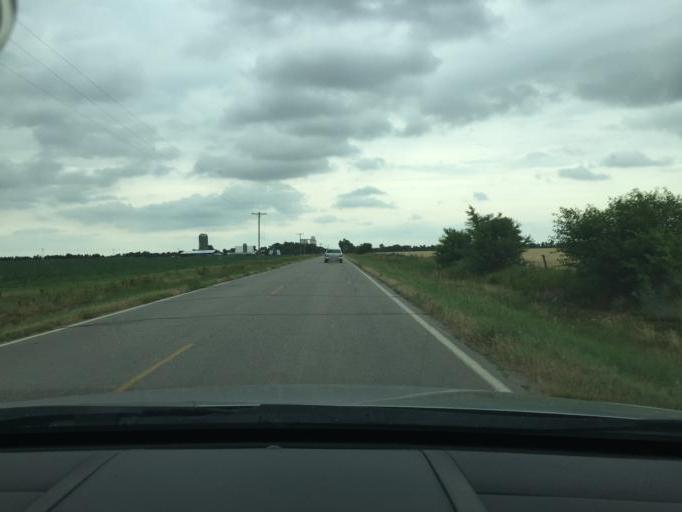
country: US
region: Kansas
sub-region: Reno County
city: South Hutchinson
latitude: 37.9921
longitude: -98.0138
